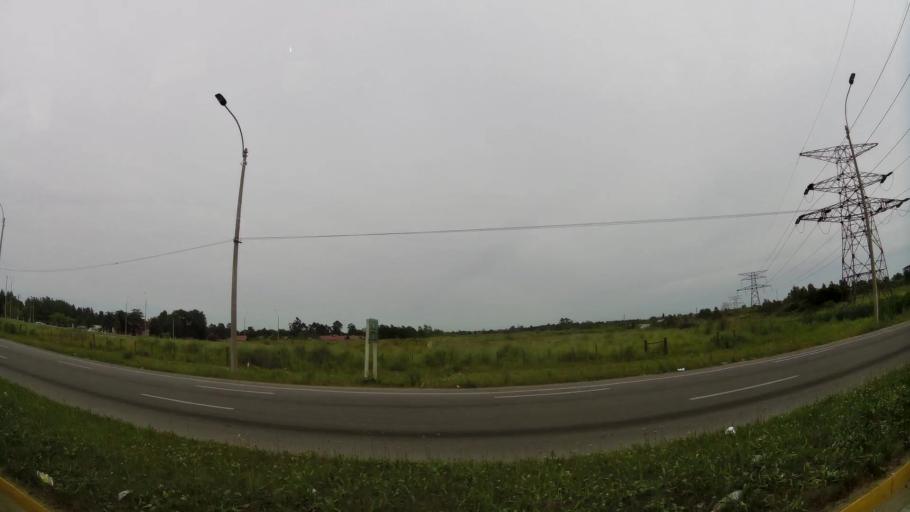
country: UY
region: Canelones
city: La Paz
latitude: -34.7829
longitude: -56.2239
